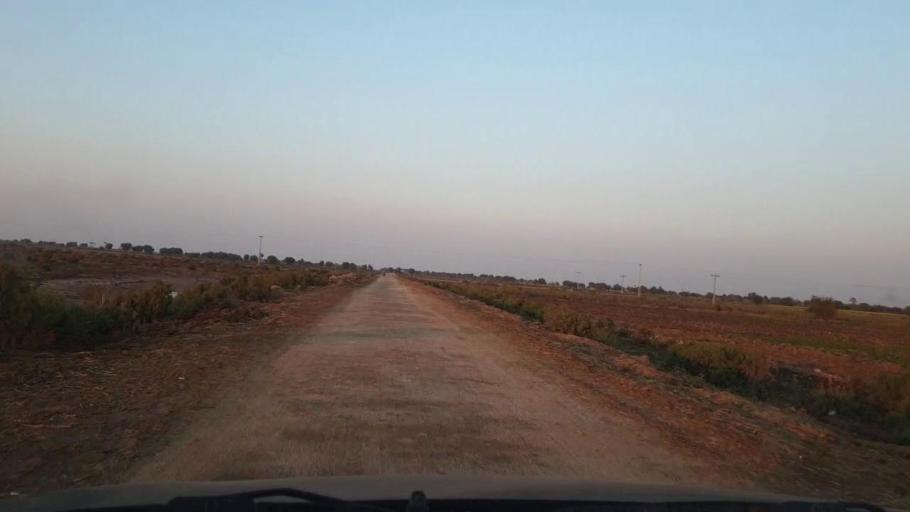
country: PK
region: Sindh
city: Jhol
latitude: 25.9290
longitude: 68.9668
